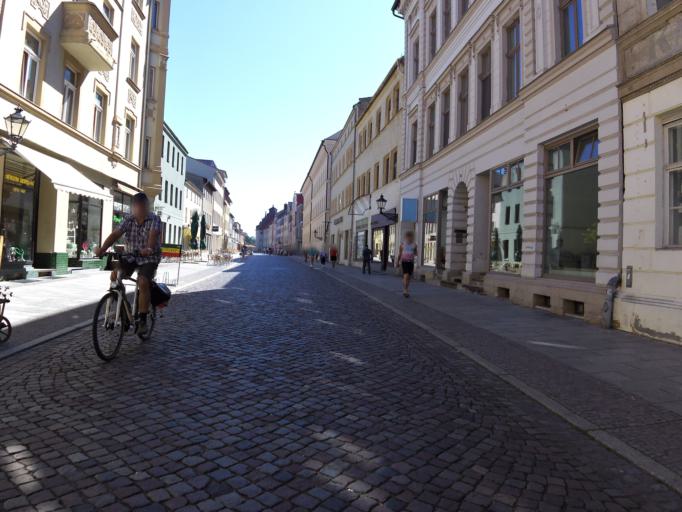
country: DE
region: Saxony-Anhalt
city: Wittenburg
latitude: 51.8652
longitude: 12.6493
